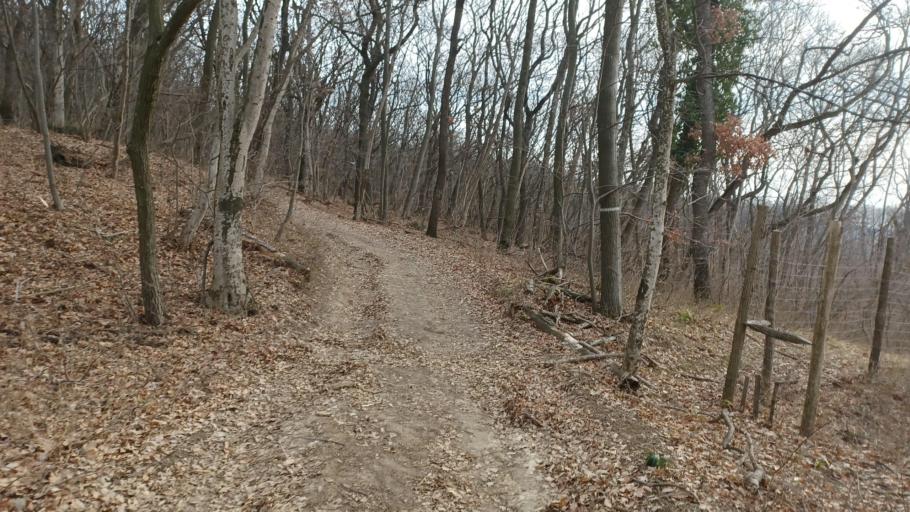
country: HU
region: Tolna
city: Szentgalpuszta
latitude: 46.3349
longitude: 18.6253
